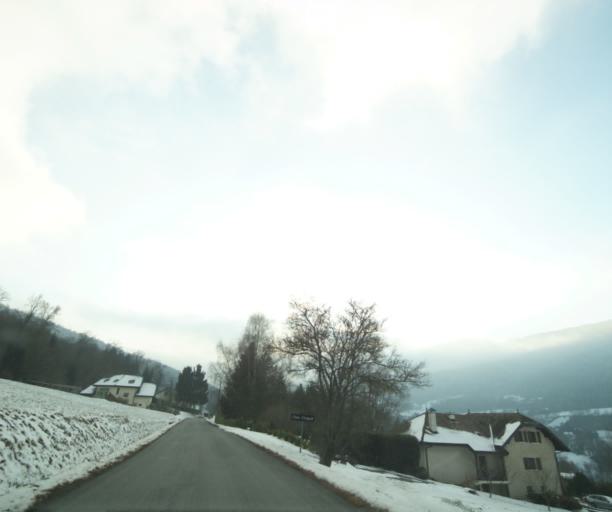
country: FR
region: Rhone-Alpes
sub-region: Departement de la Haute-Savoie
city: Monnetier-Mornex
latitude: 46.1380
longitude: 6.2245
